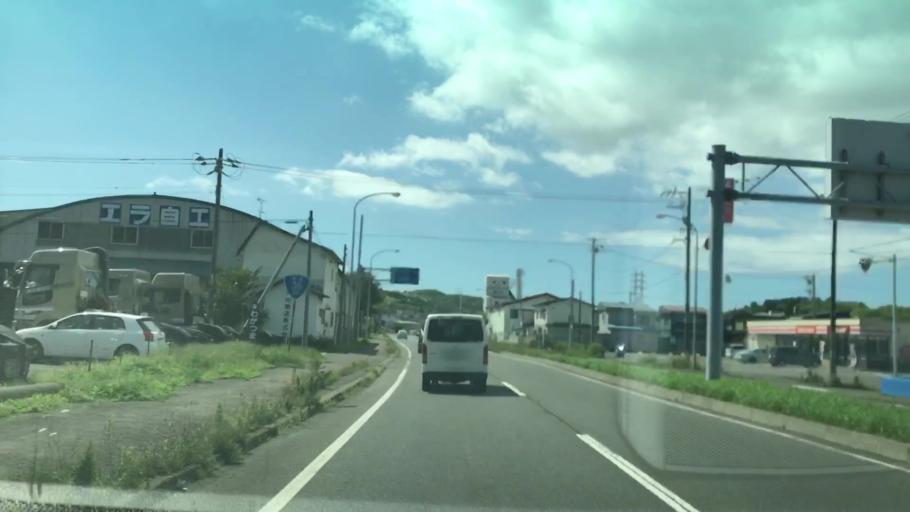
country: JP
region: Hokkaido
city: Muroran
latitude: 42.3401
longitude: 141.0284
